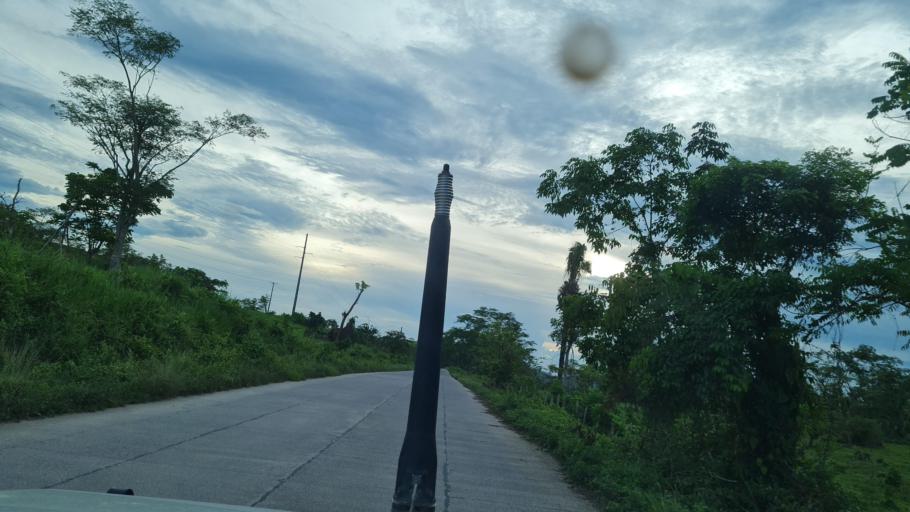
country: NI
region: Atlantico Norte (RAAN)
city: Siuna
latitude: 13.6853
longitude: -84.6034
